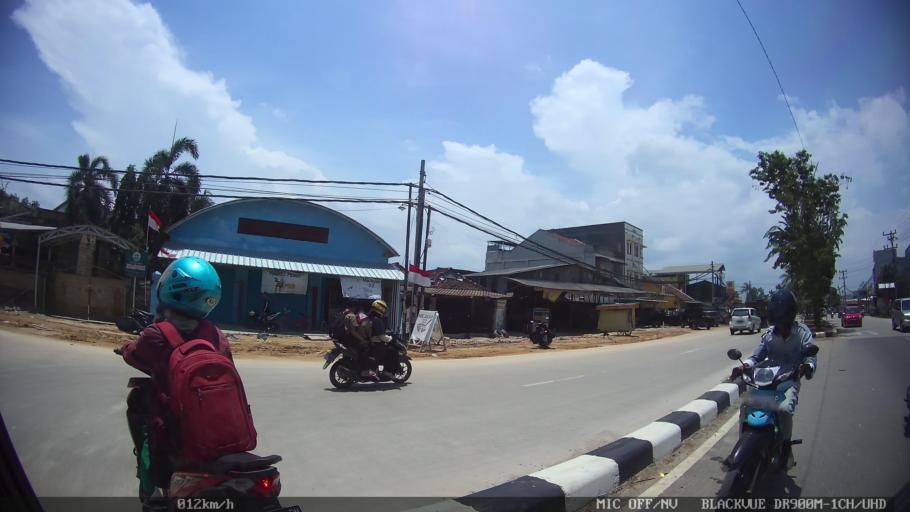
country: ID
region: Lampung
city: Kedaton
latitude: -5.3802
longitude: 105.2910
